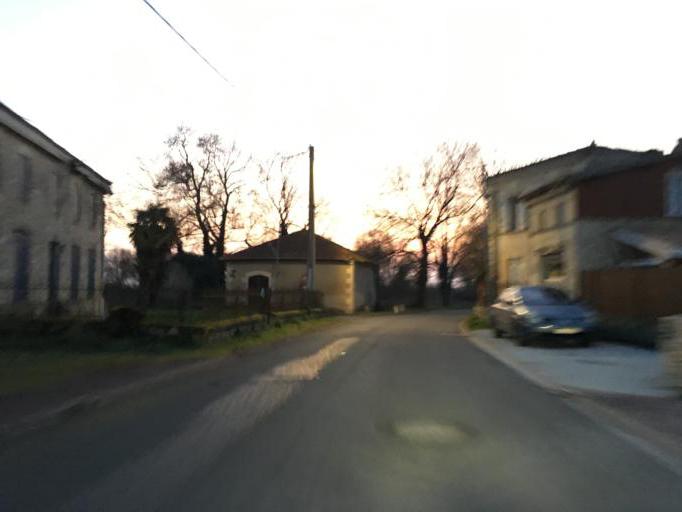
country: FR
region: Aquitaine
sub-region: Departement de la Gironde
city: Braud-et-Saint-Louis
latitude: 45.2457
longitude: -0.6387
